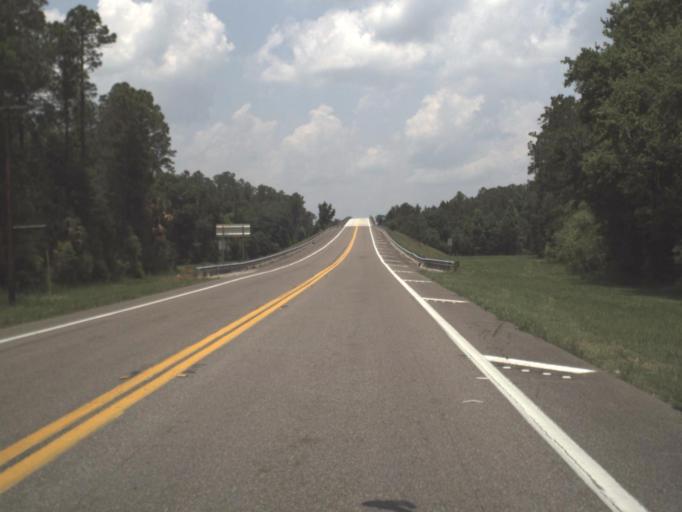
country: US
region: Florida
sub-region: Putnam County
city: Interlachen
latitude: 29.5281
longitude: -81.7544
